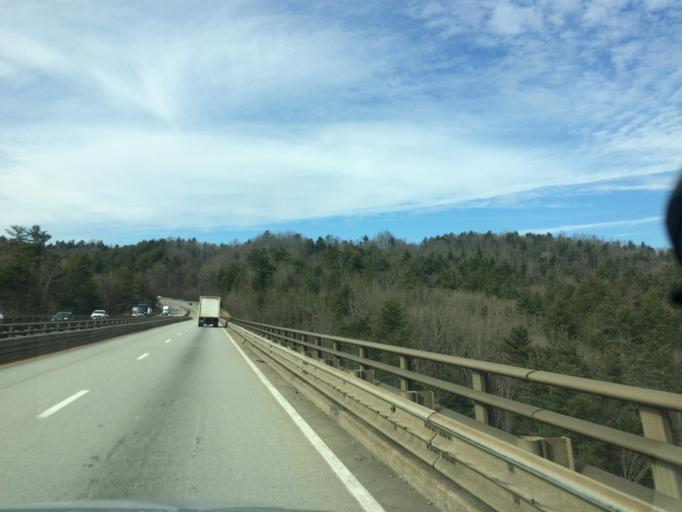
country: US
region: North Carolina
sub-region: Henderson County
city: East Flat Rock
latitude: 35.2738
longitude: -82.3727
